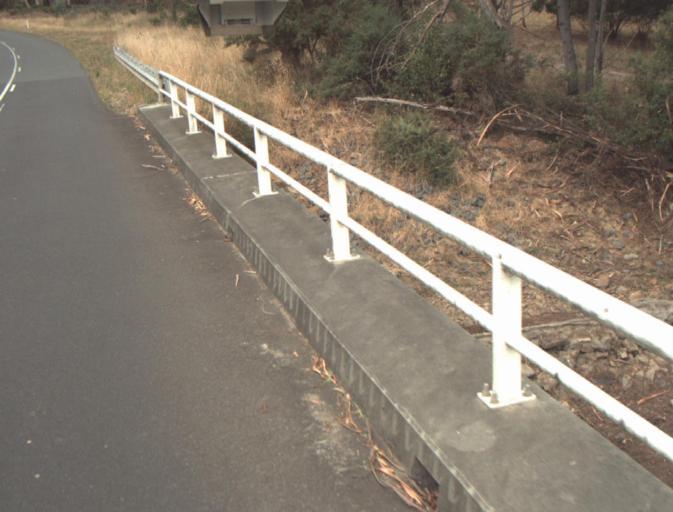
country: AU
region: Tasmania
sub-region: Northern Midlands
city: Evandale
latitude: -41.4892
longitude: 147.5023
